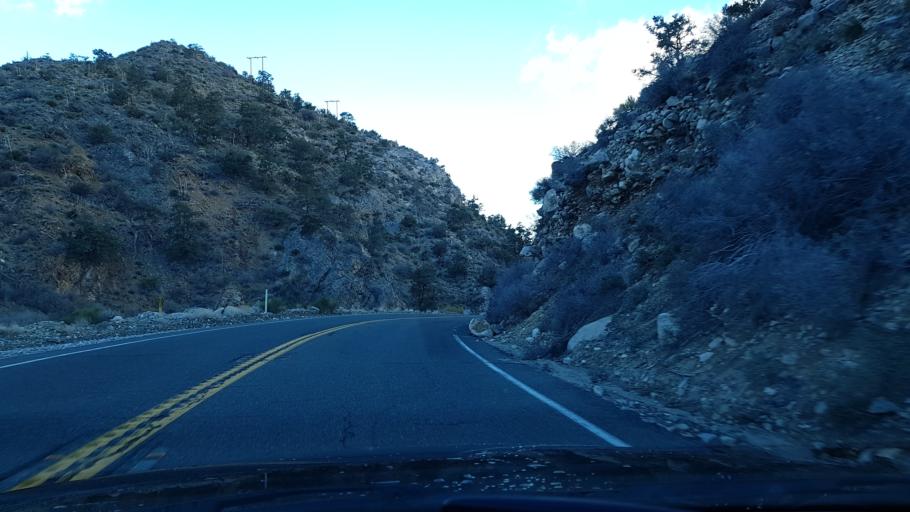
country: US
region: California
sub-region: San Bernardino County
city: Big Bear City
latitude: 34.3385
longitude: -116.8393
